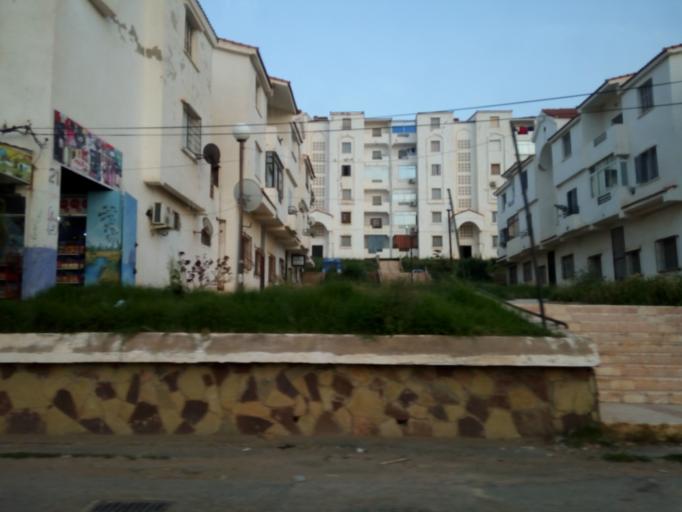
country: DZ
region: Tipaza
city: Bou Ismail
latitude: 36.6065
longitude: 2.6177
